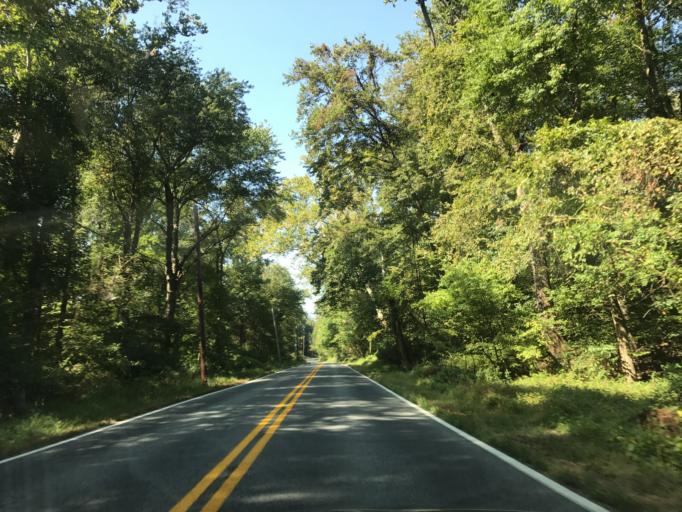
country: US
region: Maryland
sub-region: Harford County
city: Havre de Grace
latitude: 39.6296
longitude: -76.1444
